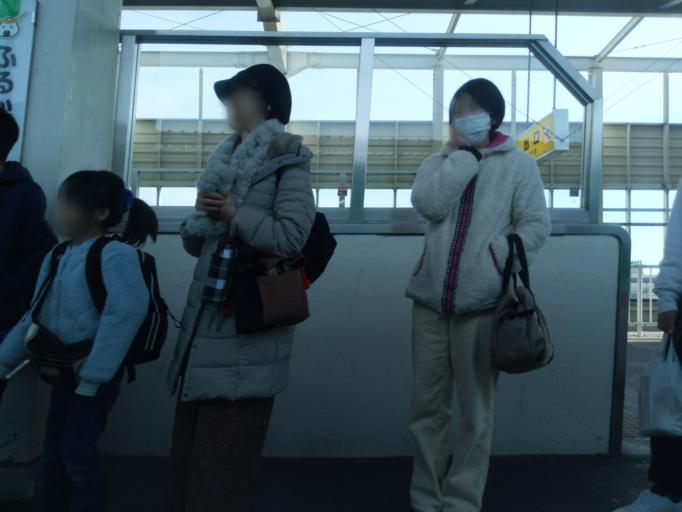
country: JP
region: Miyagi
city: Furukawa
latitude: 38.5710
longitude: 140.9680
